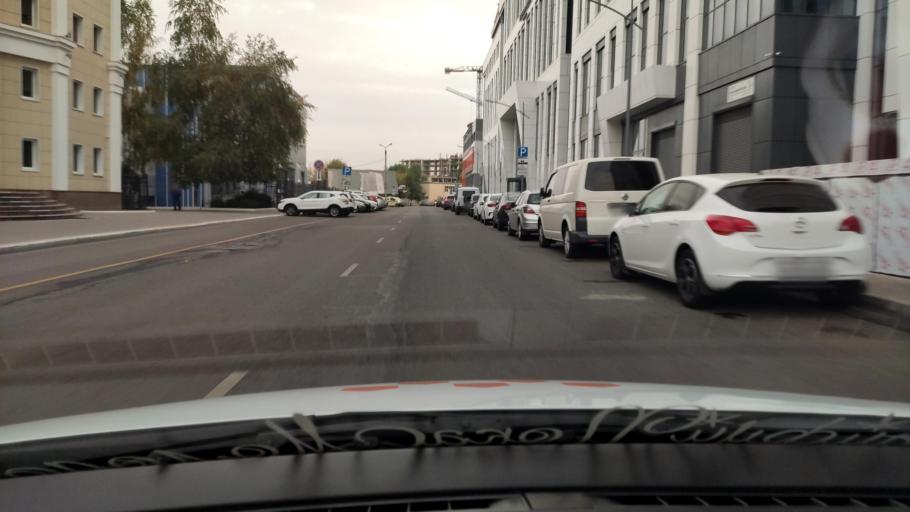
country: RU
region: Voronezj
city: Voronezh
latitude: 51.6570
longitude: 39.1927
